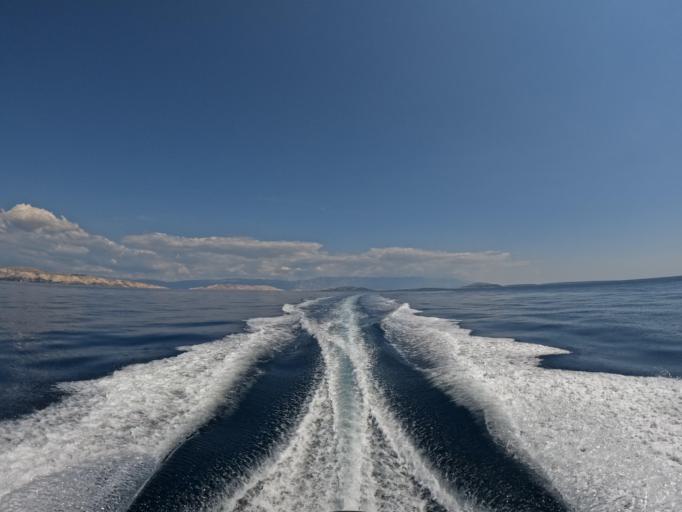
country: HR
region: Primorsko-Goranska
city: Punat
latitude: 44.9111
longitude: 14.5908
